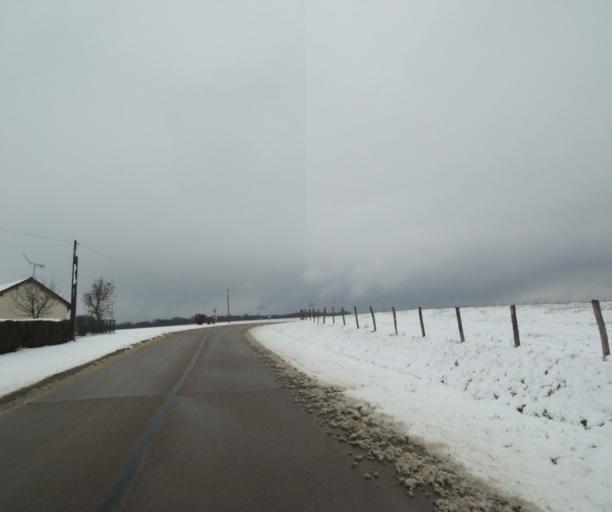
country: FR
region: Champagne-Ardenne
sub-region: Departement de la Haute-Marne
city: Laneuville-a-Remy
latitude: 48.4202
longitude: 4.8380
